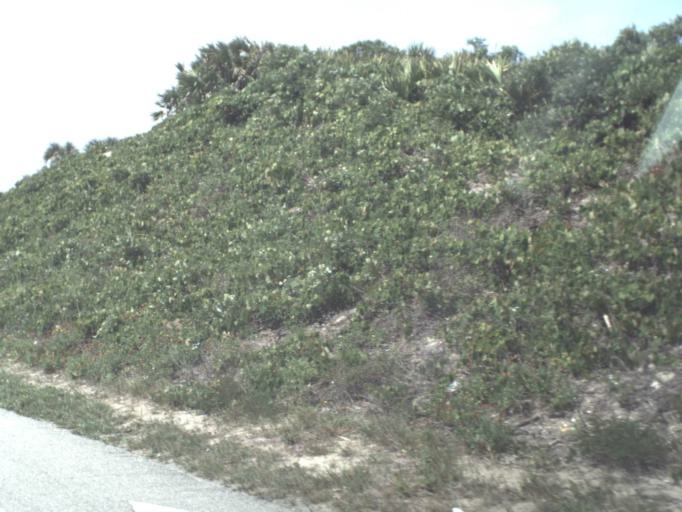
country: US
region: Florida
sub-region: Saint Johns County
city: Palm Valley
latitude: 30.1211
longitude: -81.3468
